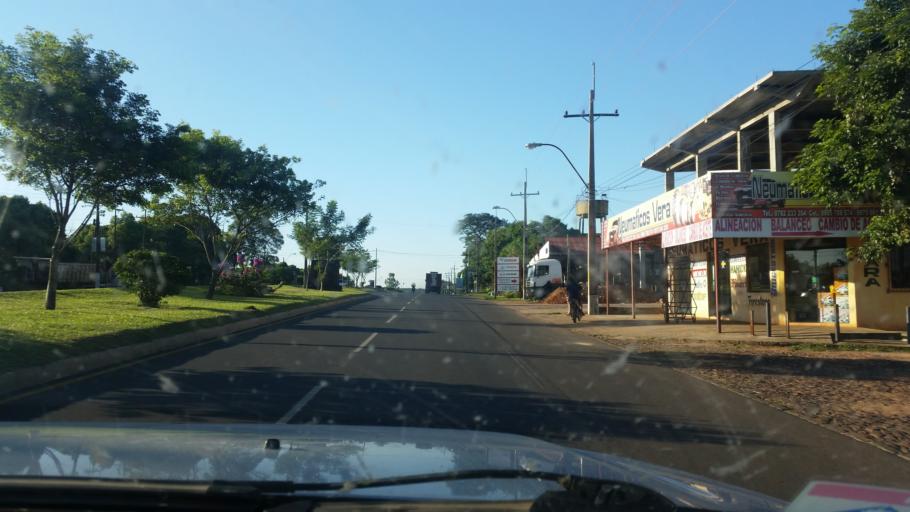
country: PY
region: Misiones
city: Santa Maria
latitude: -26.8805
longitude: -57.0319
